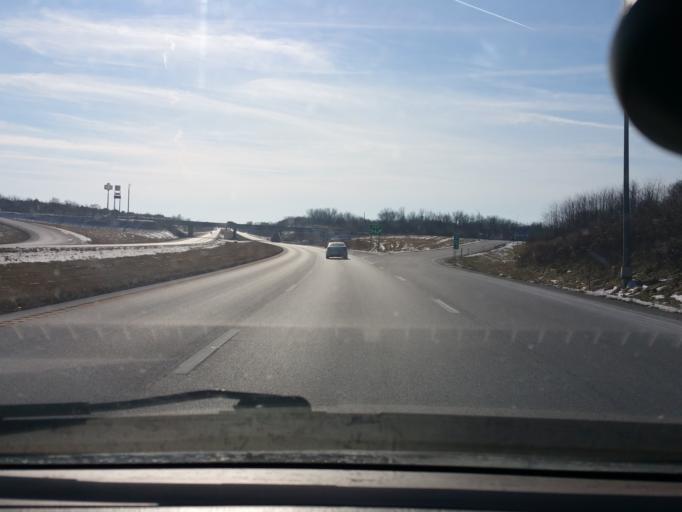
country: US
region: Missouri
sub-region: Clinton County
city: Cameron
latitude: 39.7571
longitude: -94.2197
